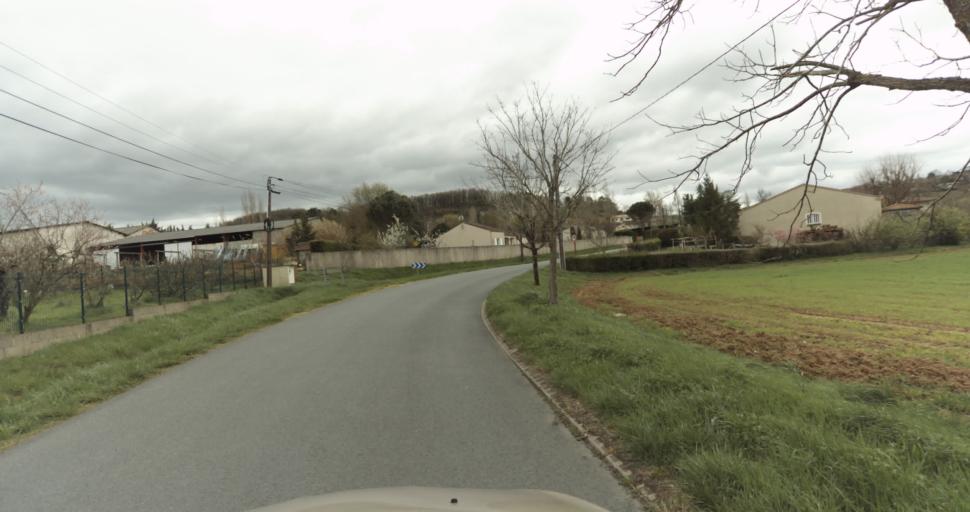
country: FR
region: Midi-Pyrenees
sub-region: Departement du Tarn
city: Puygouzon
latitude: 43.9073
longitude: 2.1729
